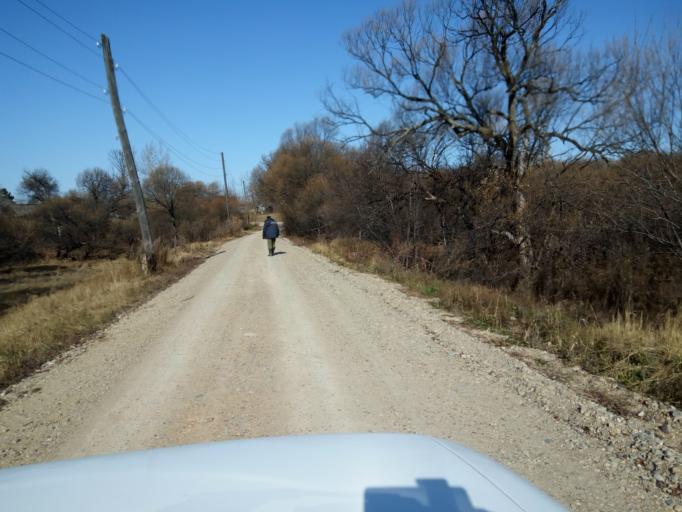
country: RU
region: Primorskiy
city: Lazo
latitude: 45.8817
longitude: 133.6416
